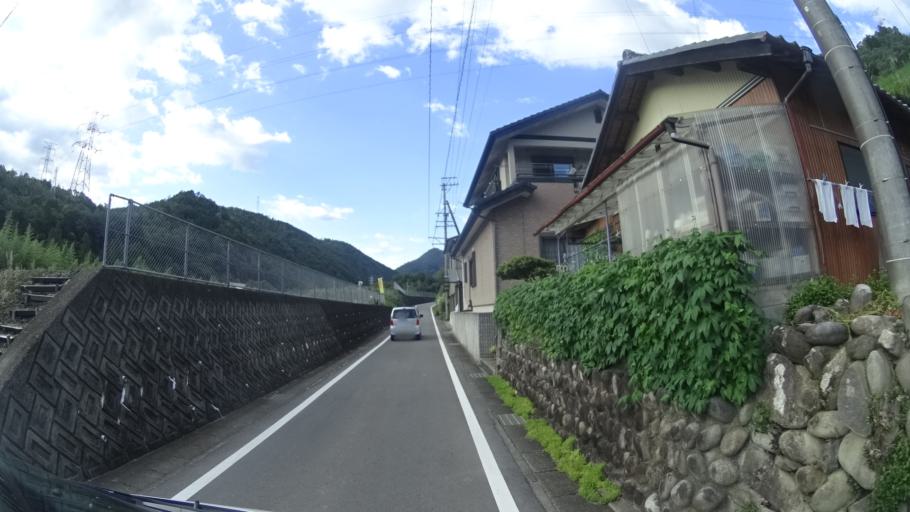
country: JP
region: Gifu
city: Minokamo
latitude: 35.5267
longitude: 137.1164
